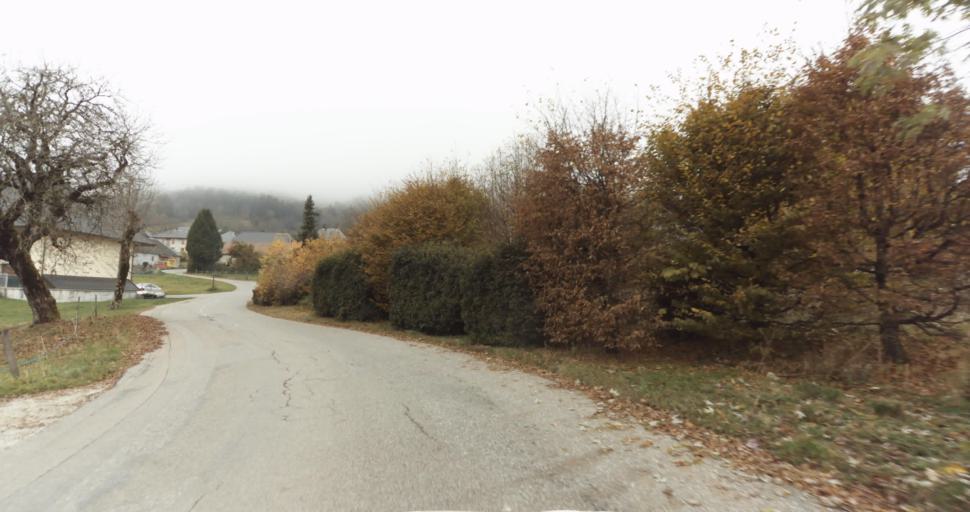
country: FR
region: Rhone-Alpes
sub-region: Departement de la Haute-Savoie
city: Saint-Jorioz
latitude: 45.7740
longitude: 6.1290
